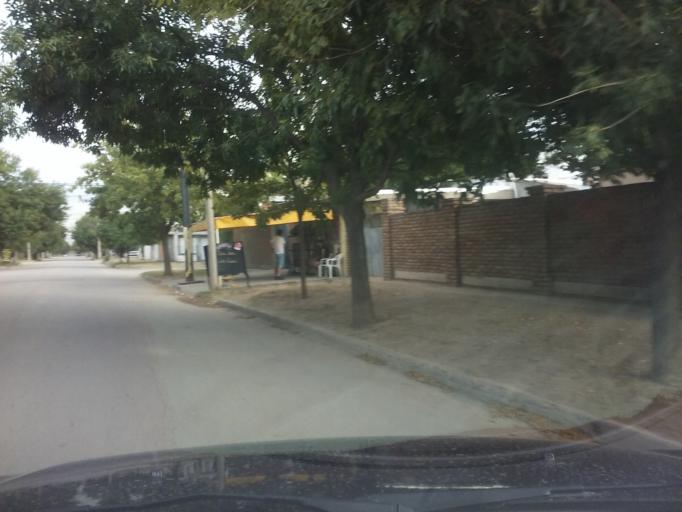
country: AR
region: La Pampa
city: Santa Rosa
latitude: -36.6489
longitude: -64.2950
